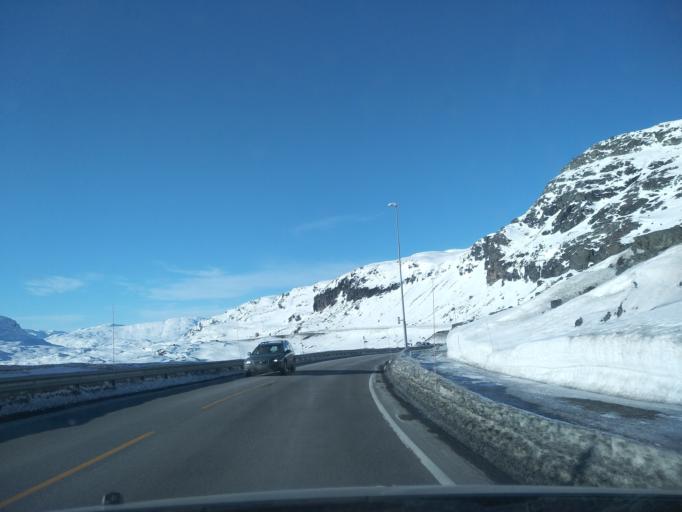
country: NO
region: Aust-Agder
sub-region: Bykle
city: Hovden
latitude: 59.8425
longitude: 6.9761
